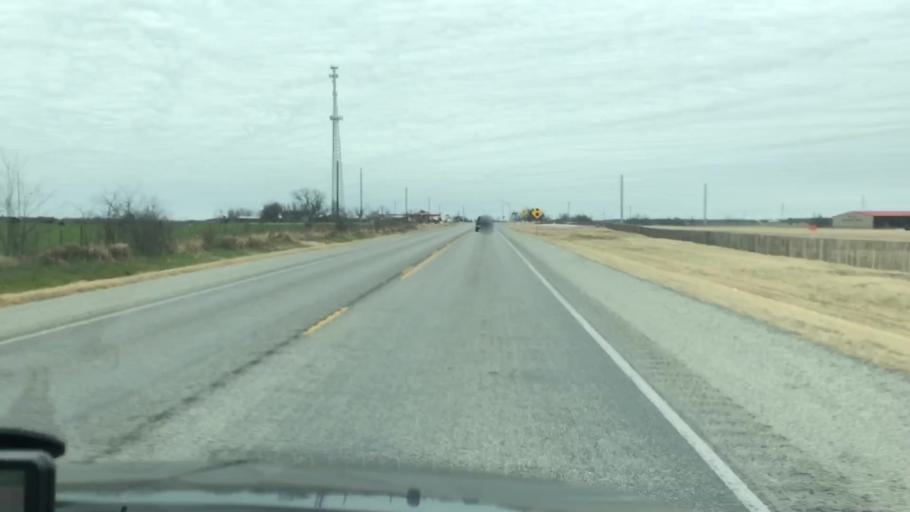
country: US
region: Texas
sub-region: Palo Pinto County
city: Mineral Wells
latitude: 32.9164
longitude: -98.0767
